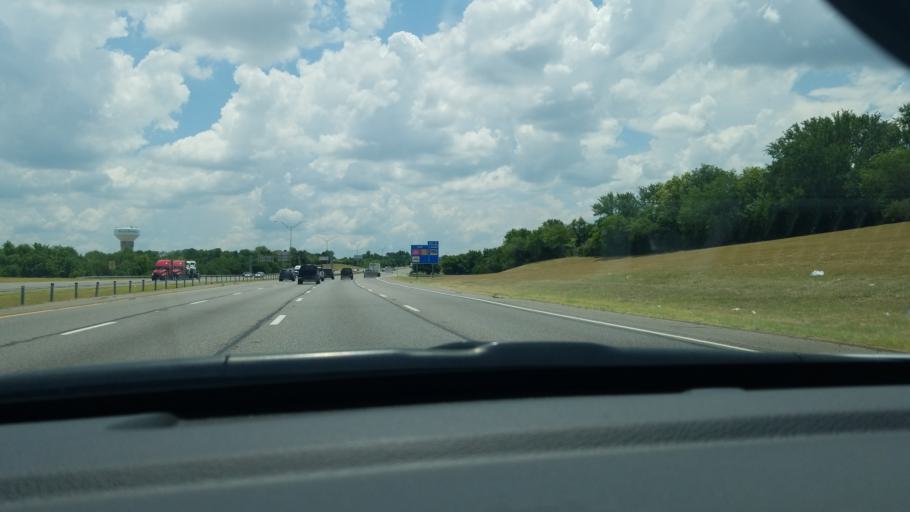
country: US
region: Texas
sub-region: Dallas County
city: Balch Springs
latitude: 32.7477
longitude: -96.6137
